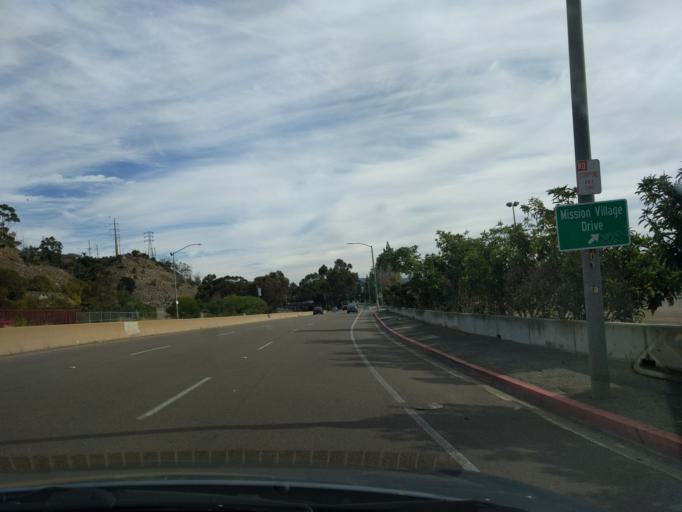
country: US
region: California
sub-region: San Diego County
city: San Diego
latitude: 32.7861
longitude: -117.1238
